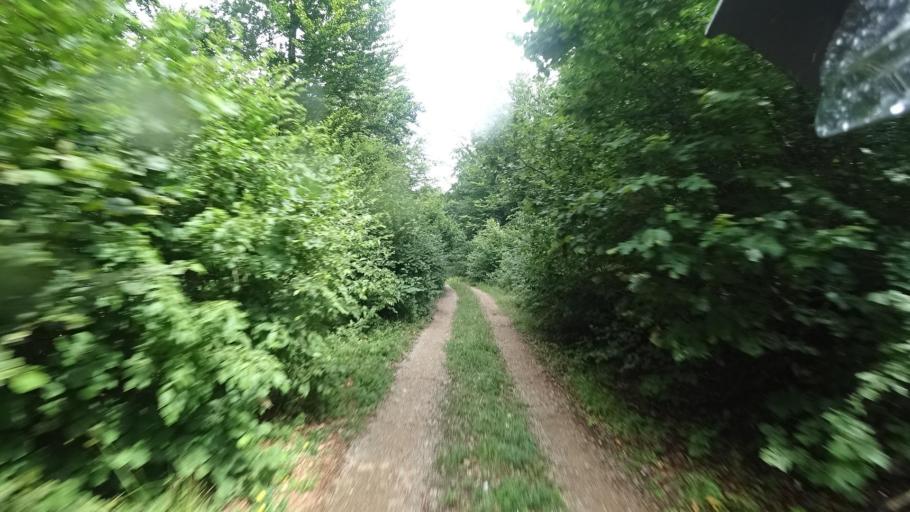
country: BA
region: Federation of Bosnia and Herzegovina
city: Bihac
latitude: 44.6518
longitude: 15.7647
